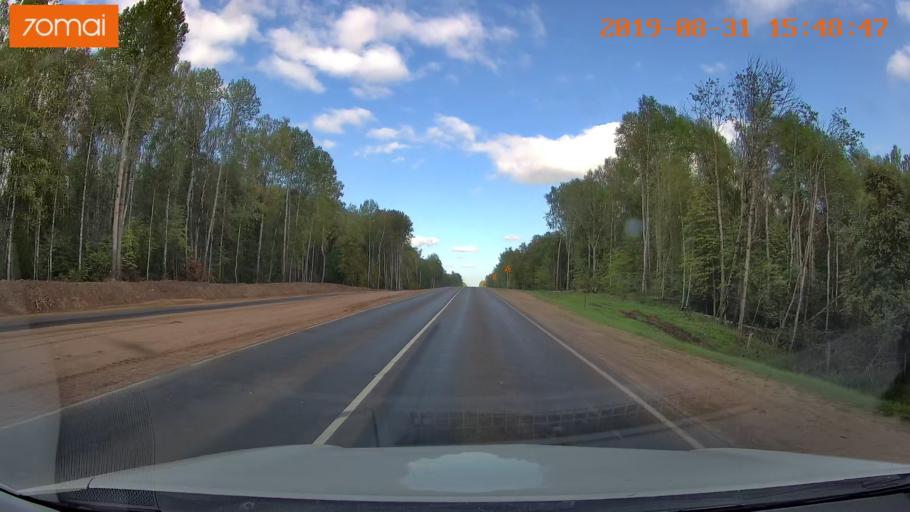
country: RU
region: Kaluga
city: Yukhnov
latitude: 54.6878
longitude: 35.0387
